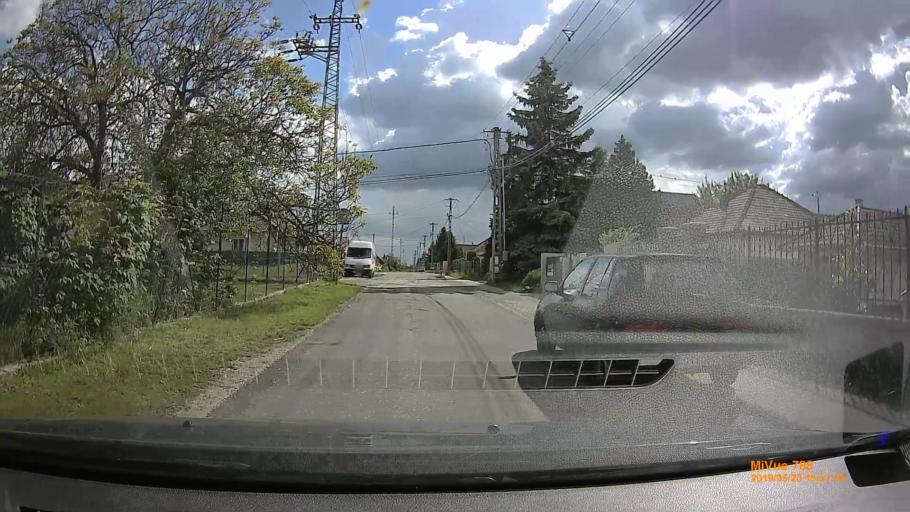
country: HU
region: Budapest
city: Budapest XVII. keruelet
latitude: 47.4714
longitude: 19.2617
